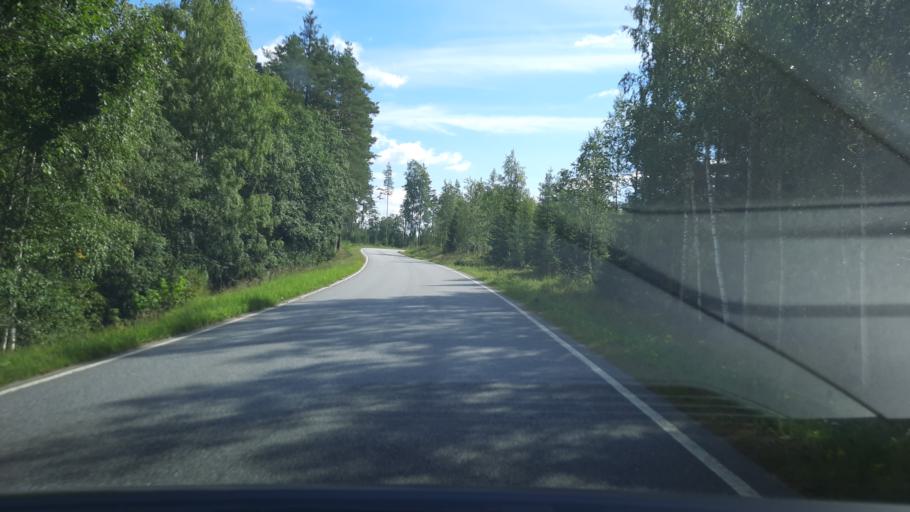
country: FI
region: Pirkanmaa
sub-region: Lounais-Pirkanmaa
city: Punkalaidun
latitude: 61.1905
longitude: 23.3139
